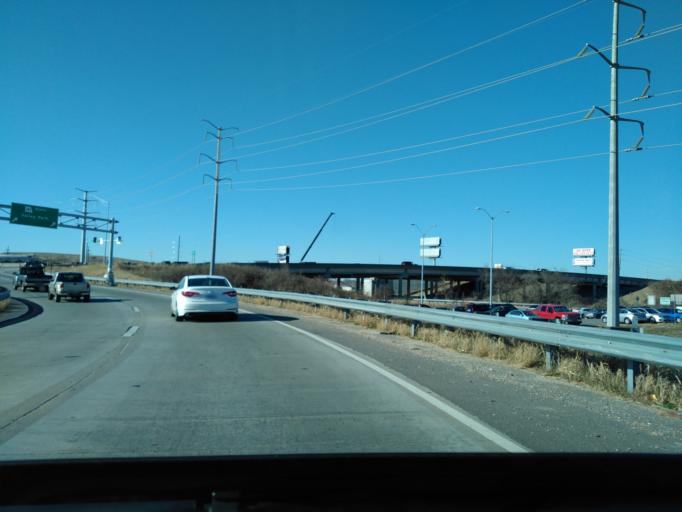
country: US
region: Missouri
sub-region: Saint Louis County
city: Valley Park
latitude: 38.5406
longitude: -90.4938
